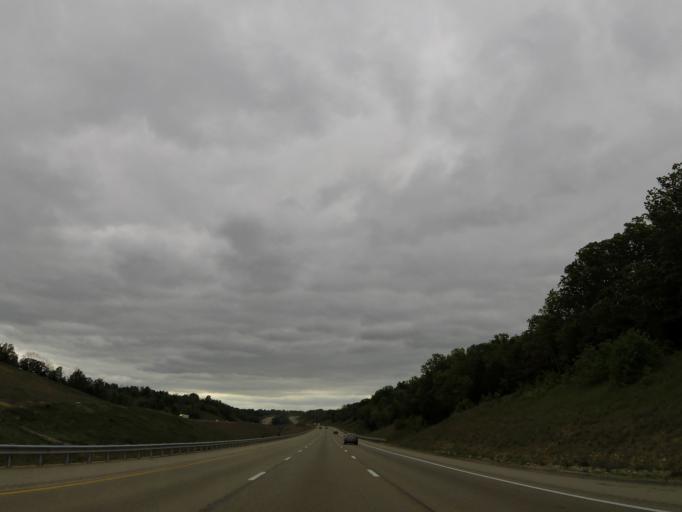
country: US
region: Kentucky
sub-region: Grant County
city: Williamstown
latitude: 38.5318
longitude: -84.5881
